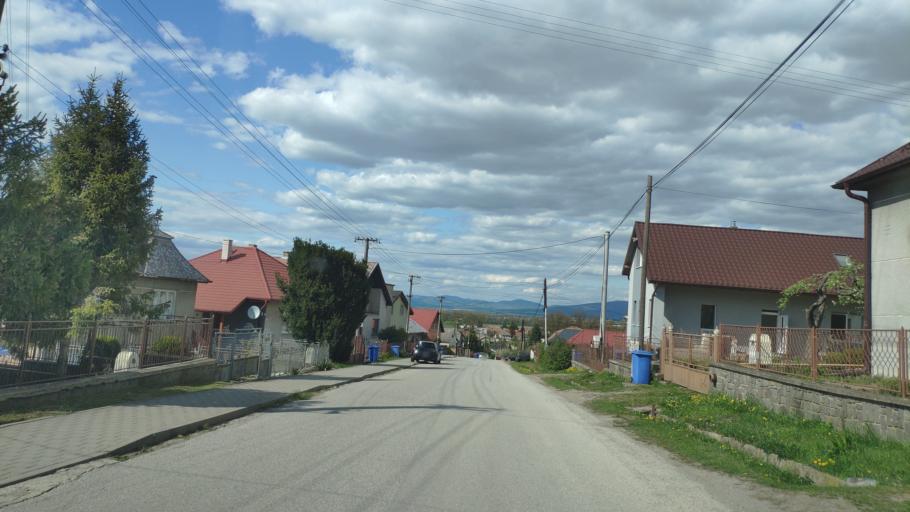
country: SK
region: Kosicky
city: Kosice
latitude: 48.6775
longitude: 21.4308
